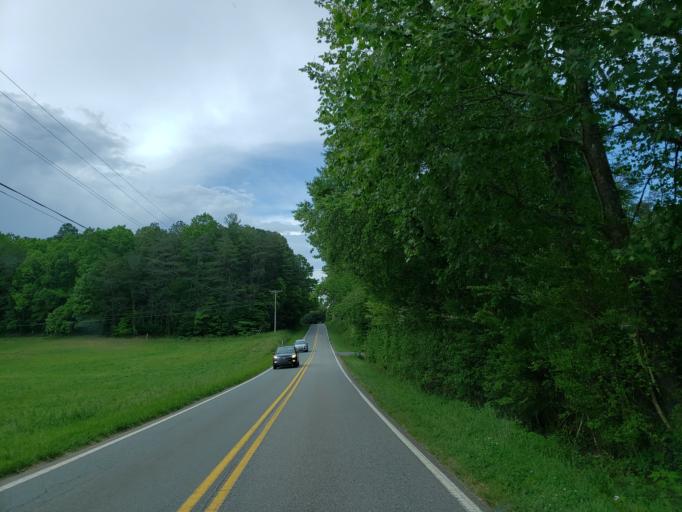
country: US
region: Georgia
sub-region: Fannin County
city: Blue Ridge
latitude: 34.8627
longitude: -84.3713
